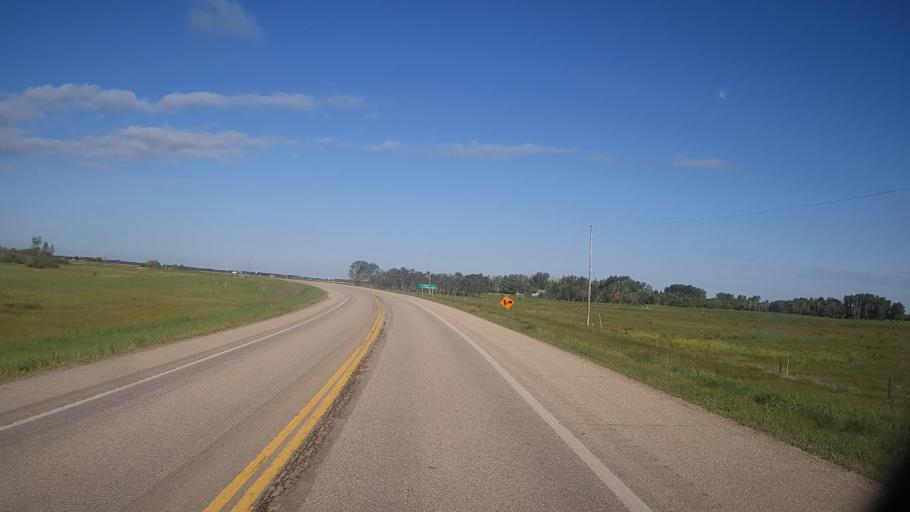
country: CA
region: Saskatchewan
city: Lanigan
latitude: 51.8750
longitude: -105.1852
